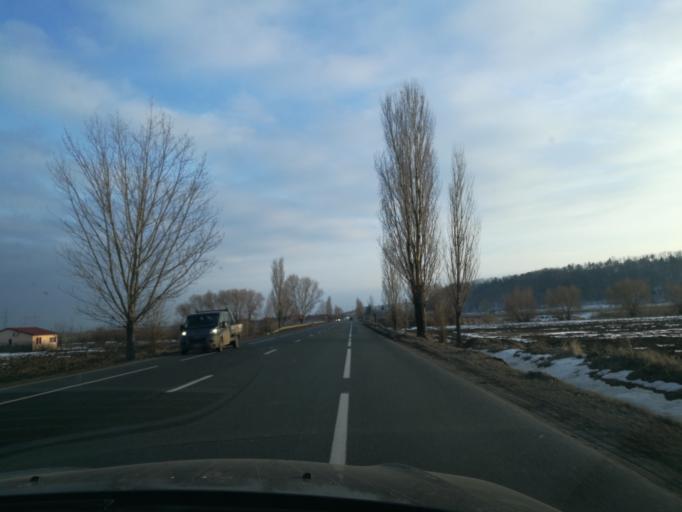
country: RO
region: Bacau
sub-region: Comuna Racaciuni
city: Racaciuni
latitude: 46.3477
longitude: 26.9964
